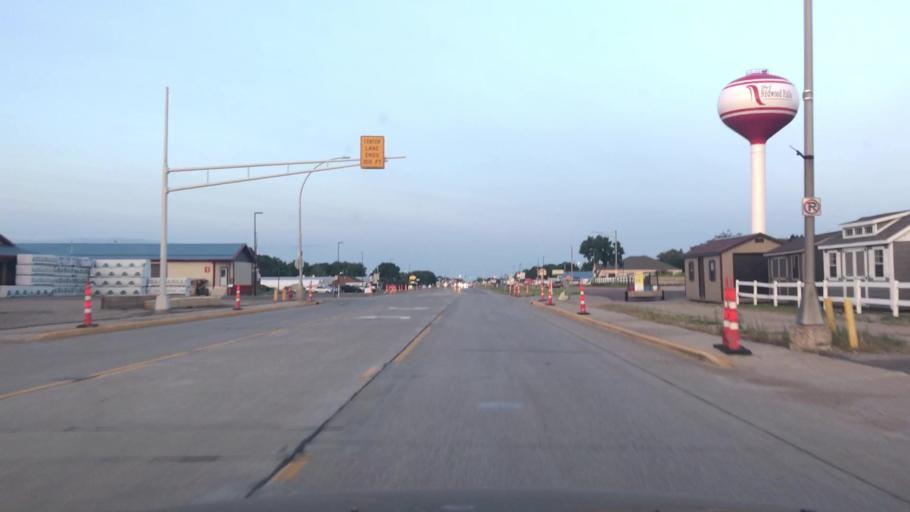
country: US
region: Minnesota
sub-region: Redwood County
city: Redwood Falls
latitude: 44.5414
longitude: -95.1074
